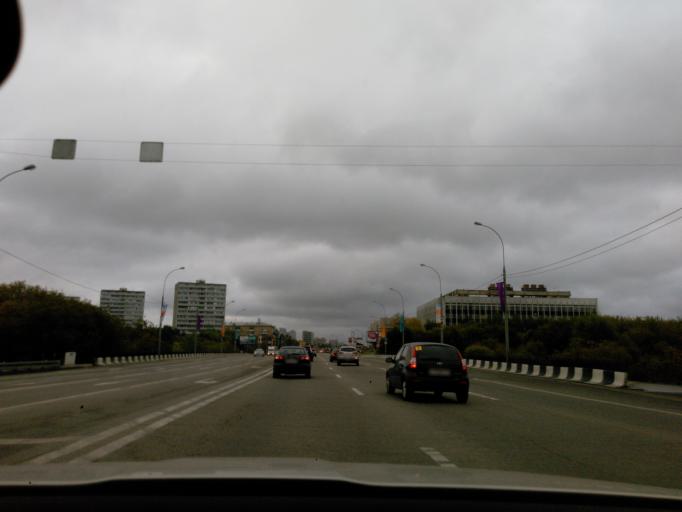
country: RU
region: Moscow
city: Strogino
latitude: 55.8279
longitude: 37.4187
